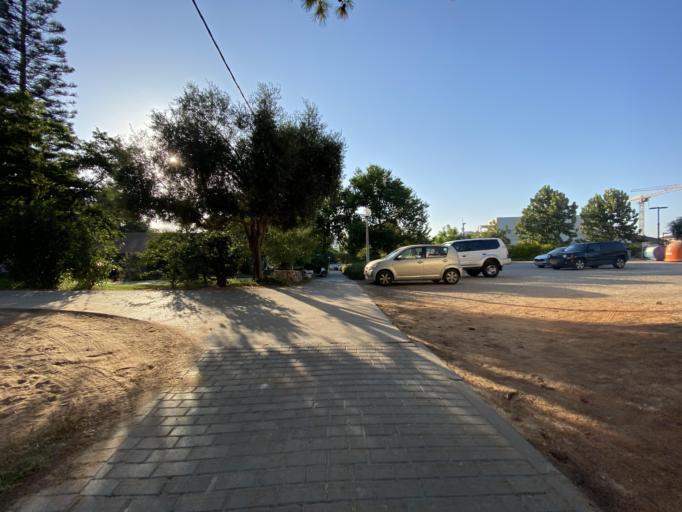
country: IL
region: Tel Aviv
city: Herzliyya
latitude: 32.1583
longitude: 34.8313
